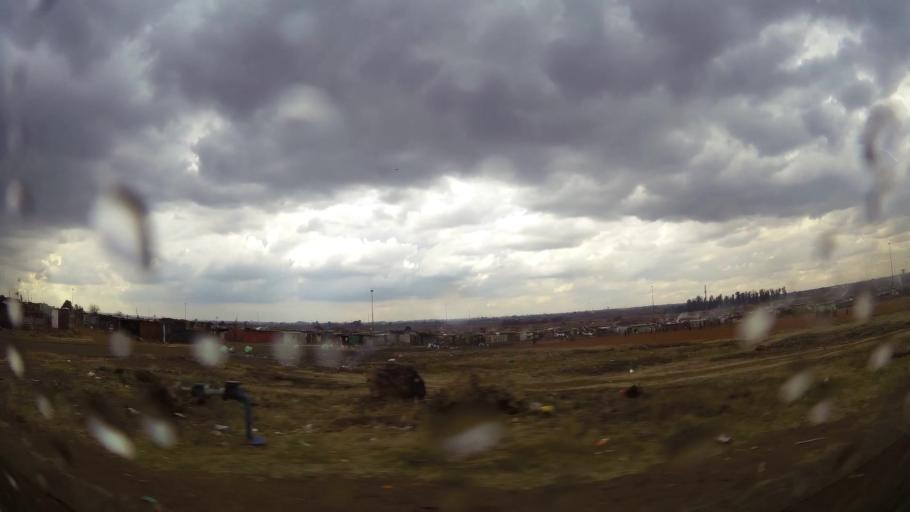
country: ZA
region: Gauteng
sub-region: Ekurhuleni Metropolitan Municipality
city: Germiston
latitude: -26.3683
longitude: 28.1653
